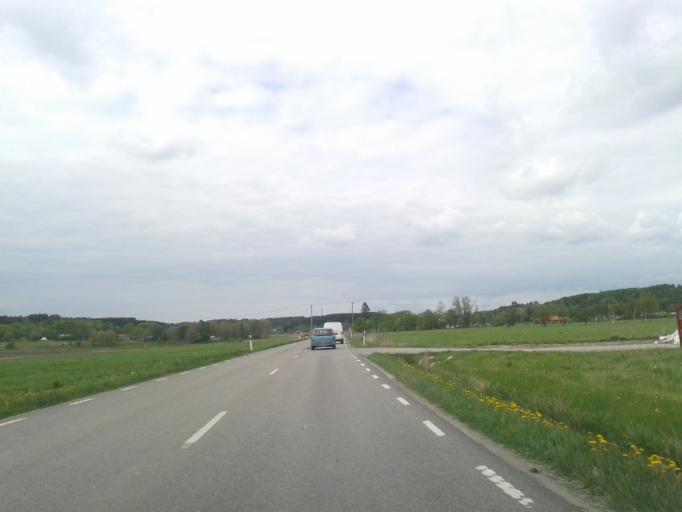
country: SE
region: Vaestra Goetaland
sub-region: Kungalvs Kommun
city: Kode
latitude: 57.8768
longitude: 11.8999
